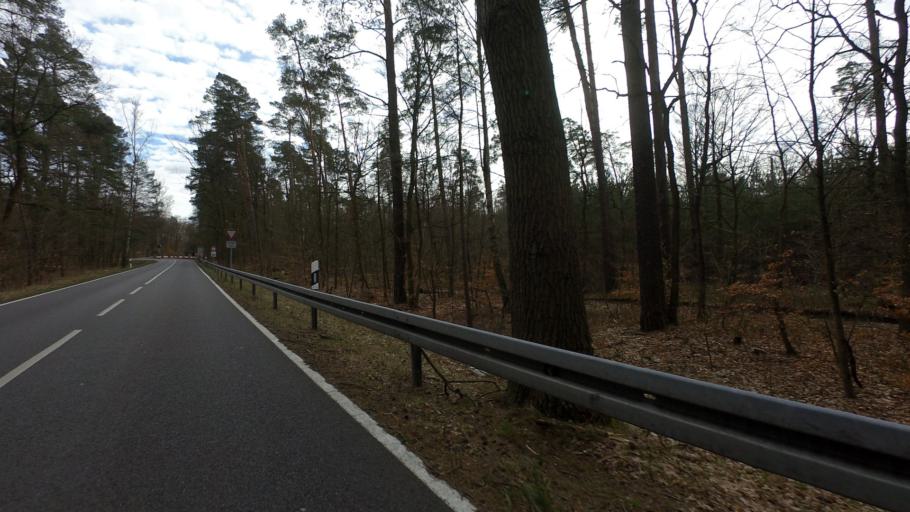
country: DE
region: Brandenburg
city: Glienicke
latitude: 52.6976
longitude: 13.3637
